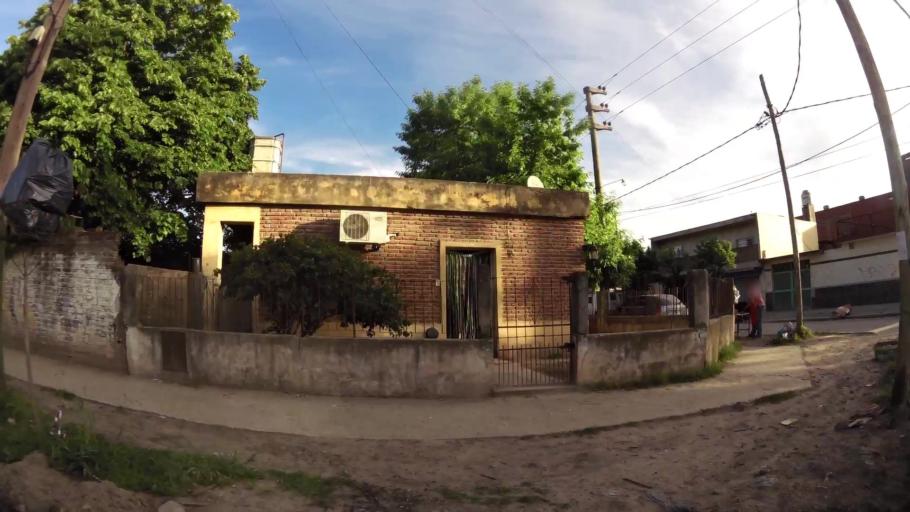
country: AR
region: Buenos Aires
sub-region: Partido de Almirante Brown
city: Adrogue
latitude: -34.7933
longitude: -58.3270
